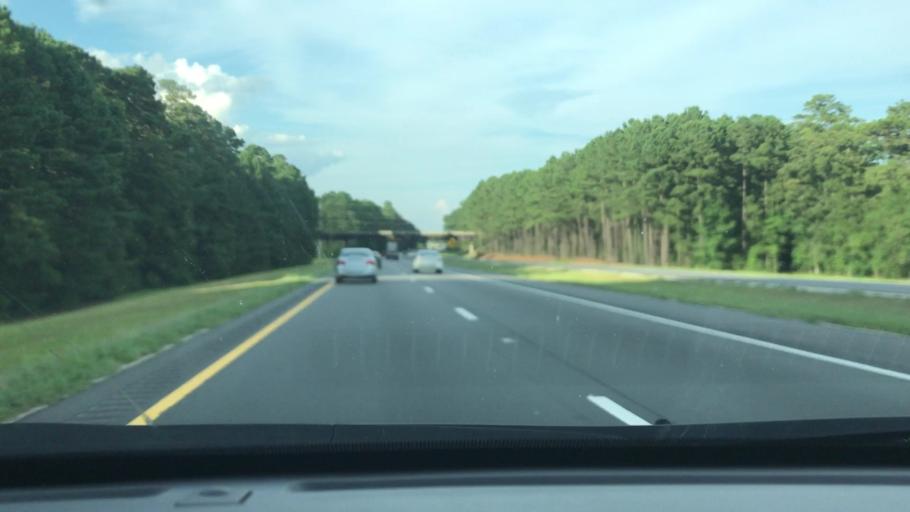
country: US
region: North Carolina
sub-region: Cumberland County
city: Fayetteville
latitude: 34.9783
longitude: -78.8540
